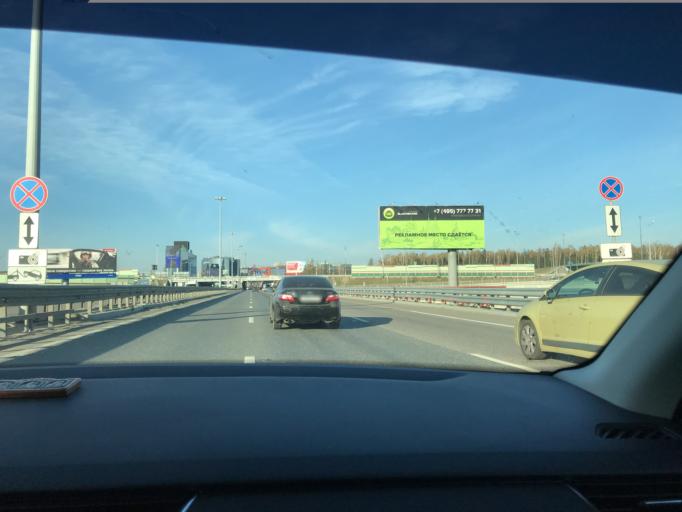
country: RU
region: Moscow
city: Khimki
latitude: 55.9539
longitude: 37.4145
